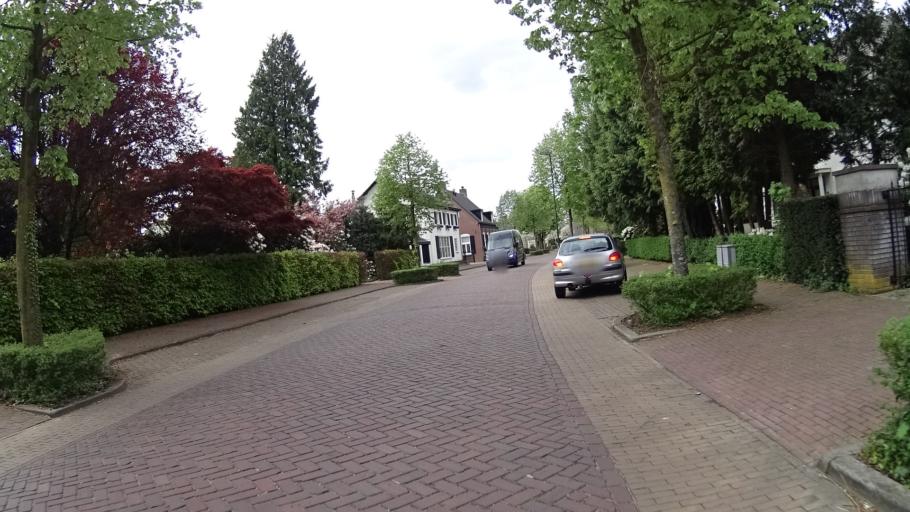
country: NL
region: North Brabant
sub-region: Gemeente Boekel
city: Boekel
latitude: 51.5496
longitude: 5.6838
